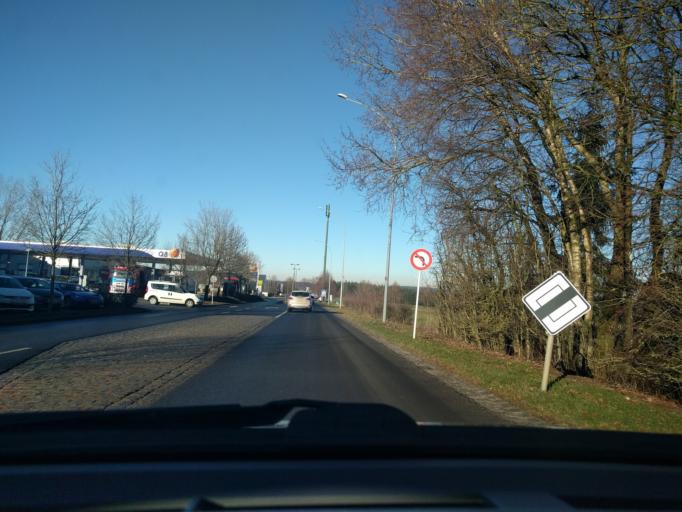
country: LU
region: Diekirch
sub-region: Canton de Clervaux
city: Troisvierges
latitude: 50.1816
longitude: 6.0233
